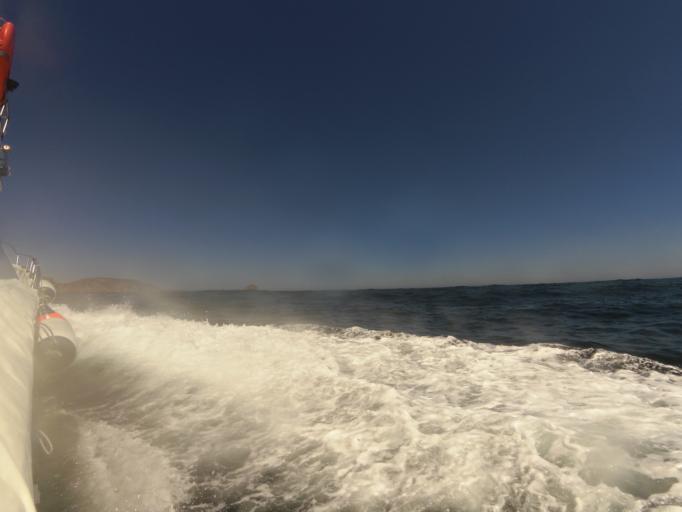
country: PT
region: Leiria
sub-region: Peniche
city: Peniche
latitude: 39.4024
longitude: -9.4905
